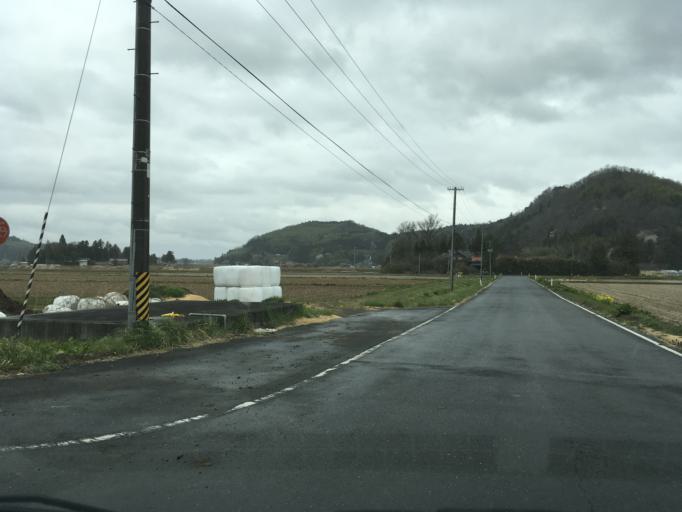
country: JP
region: Iwate
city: Ichinoseki
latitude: 38.7460
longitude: 141.2186
